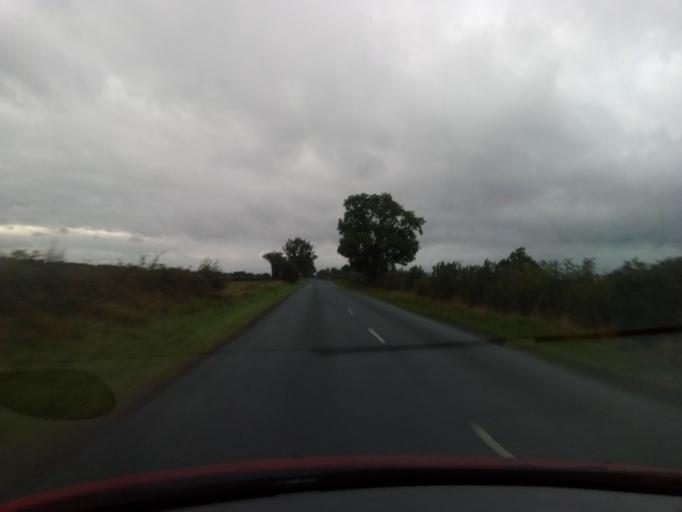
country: GB
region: England
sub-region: Darlington
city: High Coniscliffe
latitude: 54.4941
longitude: -1.6705
